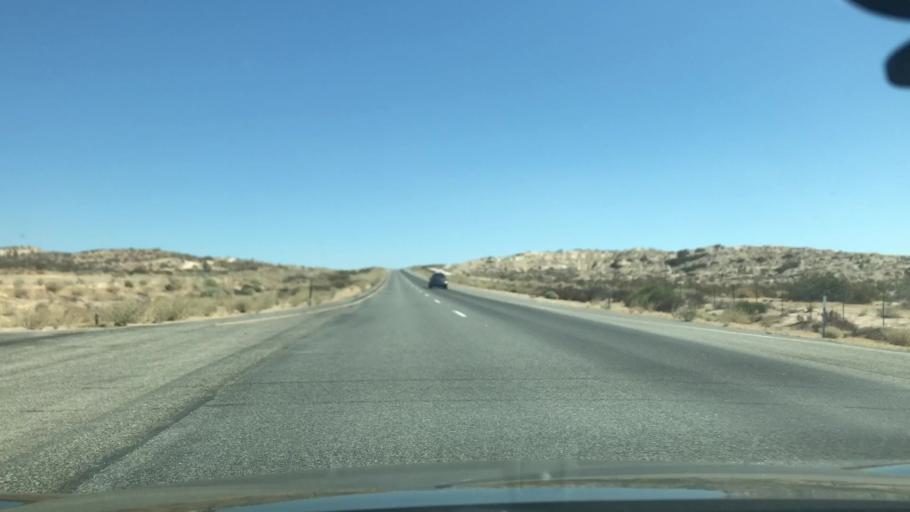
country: US
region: California
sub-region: Kern County
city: Inyokern
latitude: 35.4139
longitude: -117.9806
